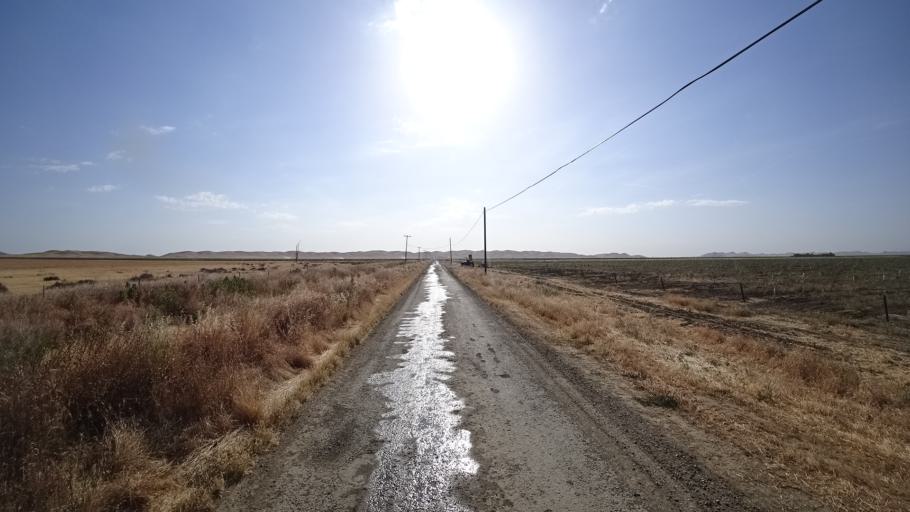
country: US
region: California
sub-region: Kings County
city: Avenal
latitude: 35.8179
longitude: -120.0708
